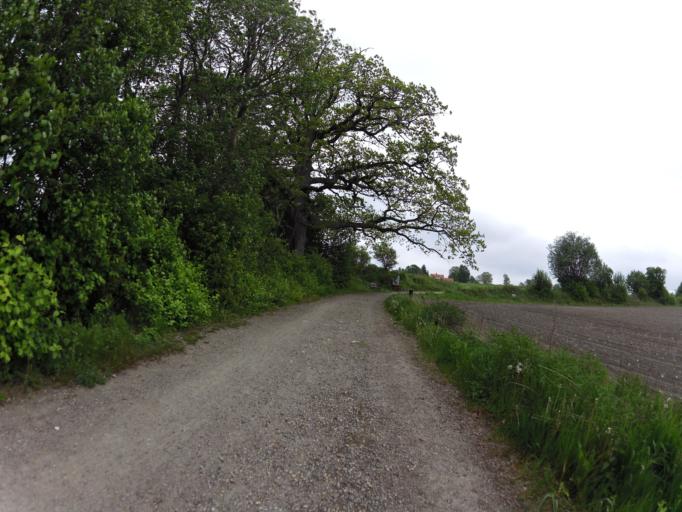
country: NO
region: Ostfold
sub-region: Moss
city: Moss
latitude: 59.3853
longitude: 10.6745
